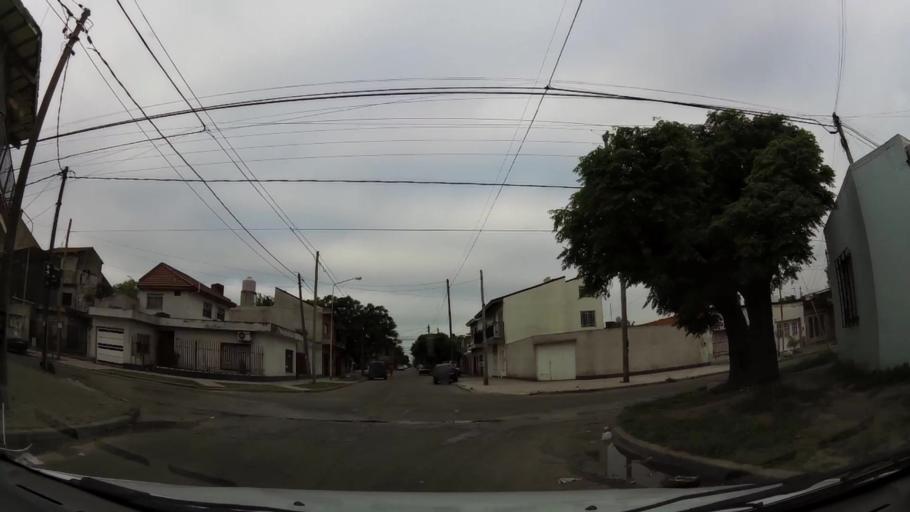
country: AR
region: Buenos Aires
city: San Justo
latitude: -34.7014
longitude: -58.5626
